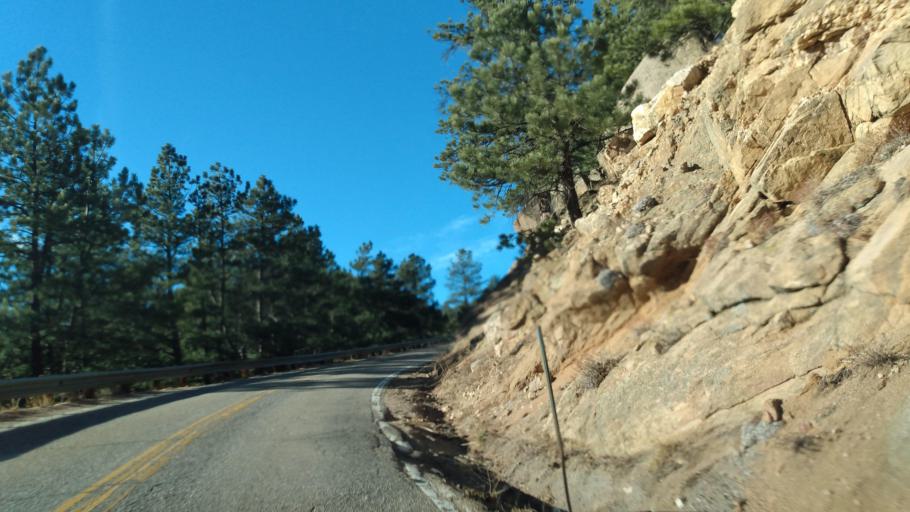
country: US
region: Colorado
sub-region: Boulder County
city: Boulder
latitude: 39.9960
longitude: -105.3581
